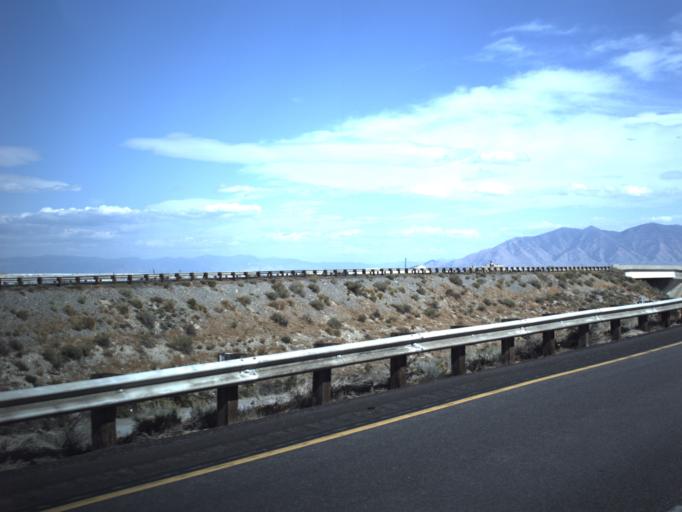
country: US
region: Utah
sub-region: Tooele County
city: Grantsville
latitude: 40.7101
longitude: -112.5319
